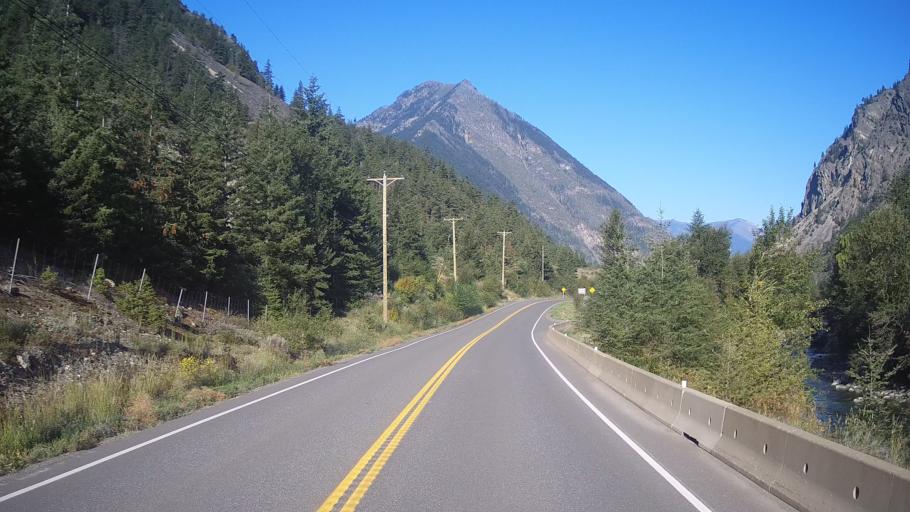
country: CA
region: British Columbia
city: Lillooet
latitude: 50.6685
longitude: -121.9619
